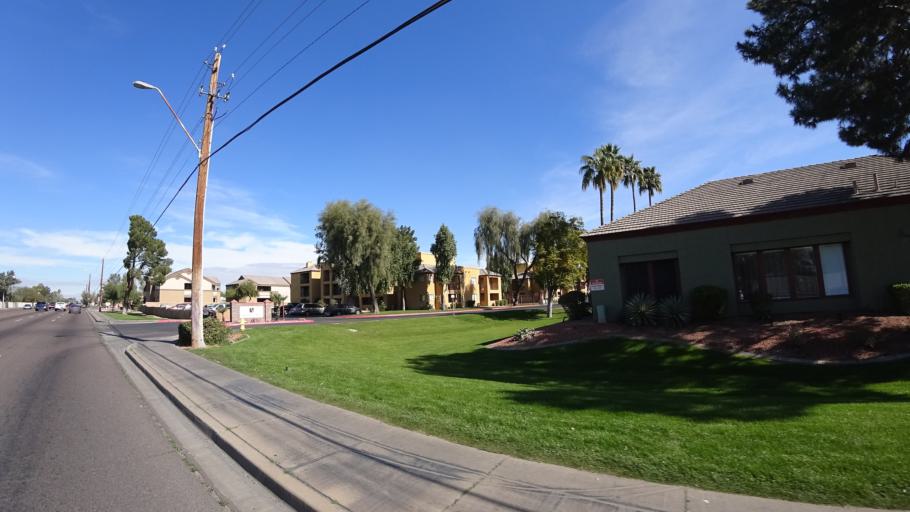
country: US
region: Arizona
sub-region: Maricopa County
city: Glendale
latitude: 33.4826
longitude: -112.2032
